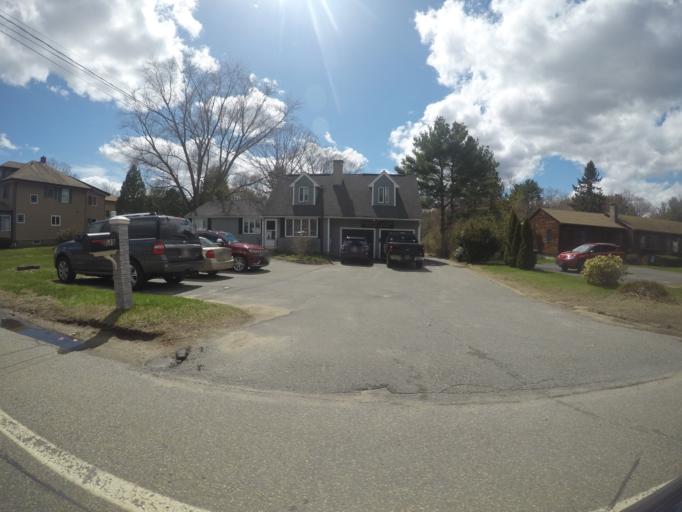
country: US
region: Massachusetts
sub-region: Plymouth County
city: West Bridgewater
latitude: 42.0255
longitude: -71.0678
